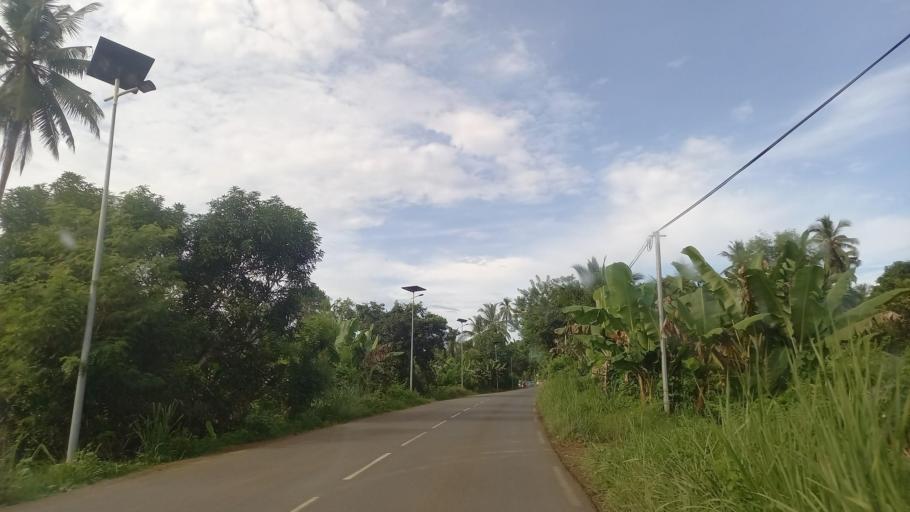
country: YT
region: Chirongui
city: Chirongui
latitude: -12.9250
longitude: 45.1552
